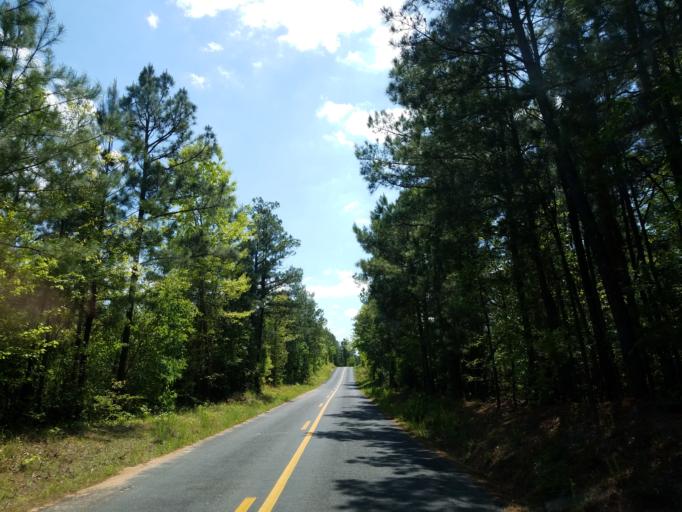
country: US
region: Georgia
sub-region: Butts County
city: Indian Springs
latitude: 33.1488
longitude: -84.0060
